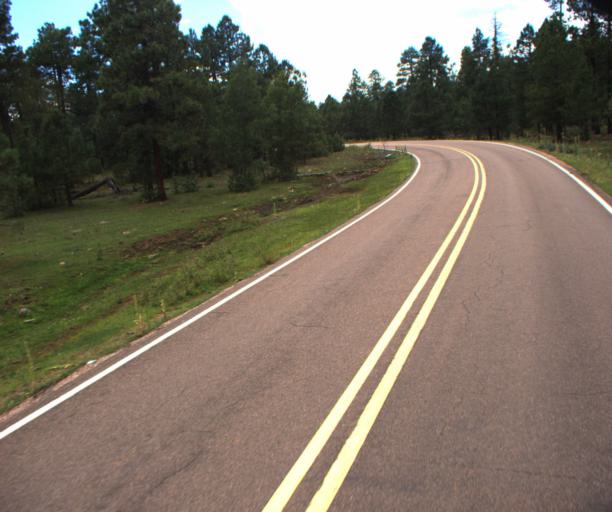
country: US
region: Arizona
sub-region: Navajo County
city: Pinetop-Lakeside
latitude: 34.0134
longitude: -109.7755
